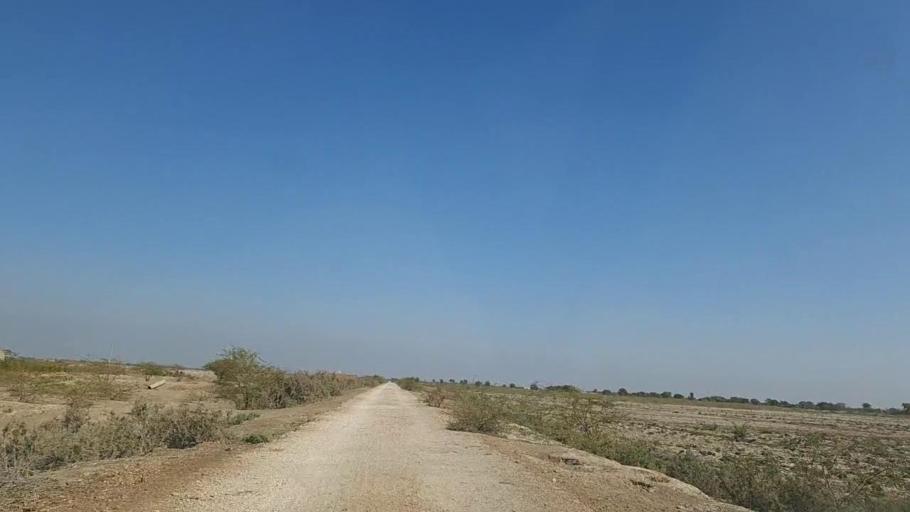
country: PK
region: Sindh
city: Samaro
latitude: 25.3991
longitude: 69.4223
